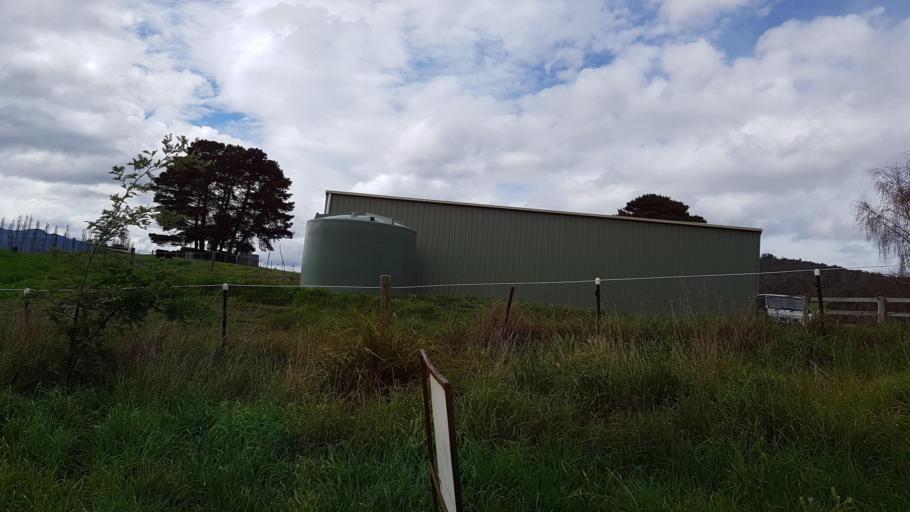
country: AU
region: Tasmania
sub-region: Huon Valley
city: Huonville
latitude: -42.9969
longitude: 147.0657
